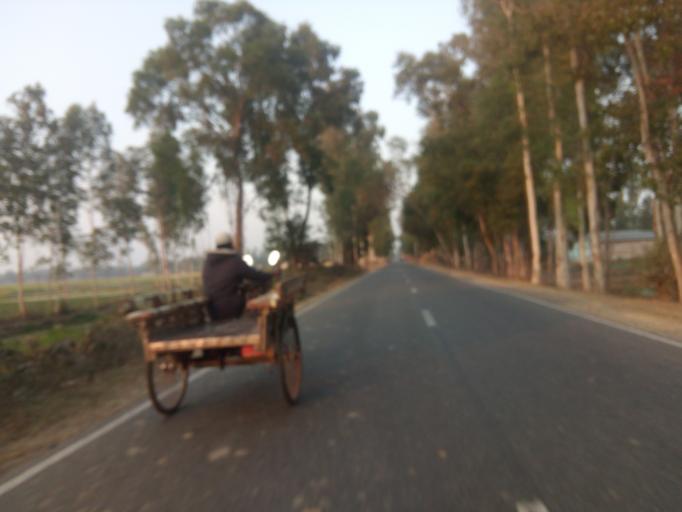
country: BD
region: Rajshahi
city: Bogra
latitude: 24.6342
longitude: 89.2479
